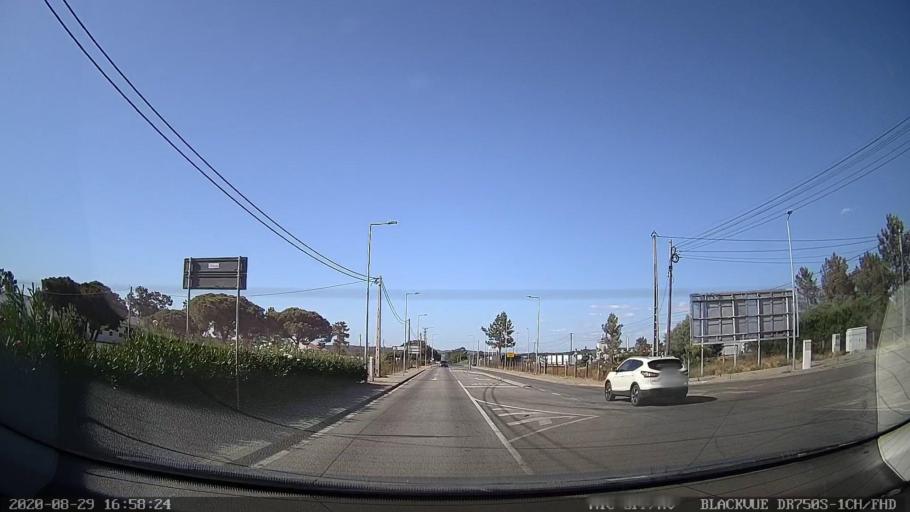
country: PT
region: Setubal
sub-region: Alcacer do Sal
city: Alcacer do Sal
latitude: 38.3958
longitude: -8.5142
